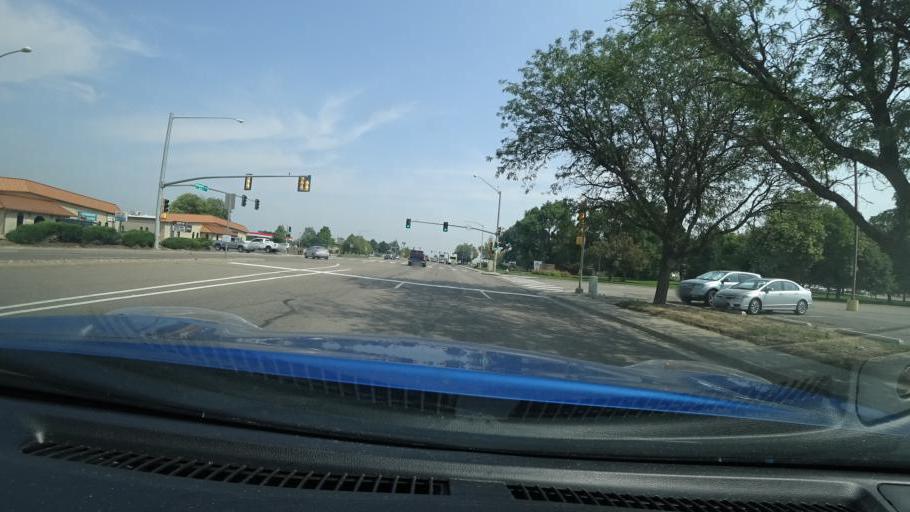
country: US
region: Colorado
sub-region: Adams County
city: Aurora
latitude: 39.7235
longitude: -104.7911
